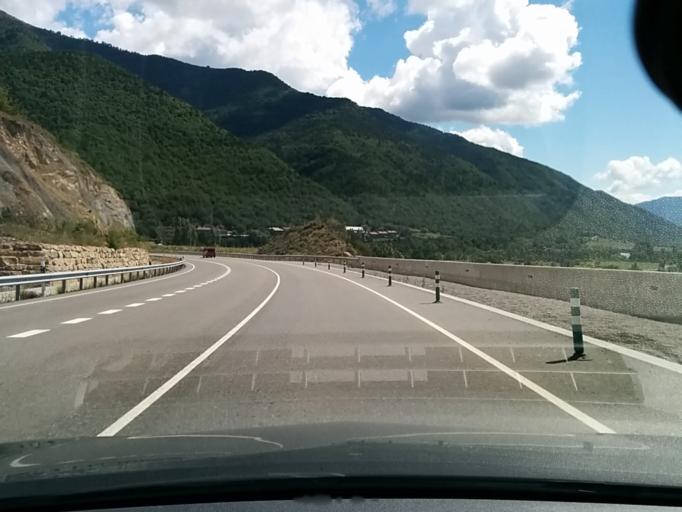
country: ES
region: Aragon
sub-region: Provincia de Huesca
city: Fiscal
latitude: 42.4967
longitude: -0.1241
